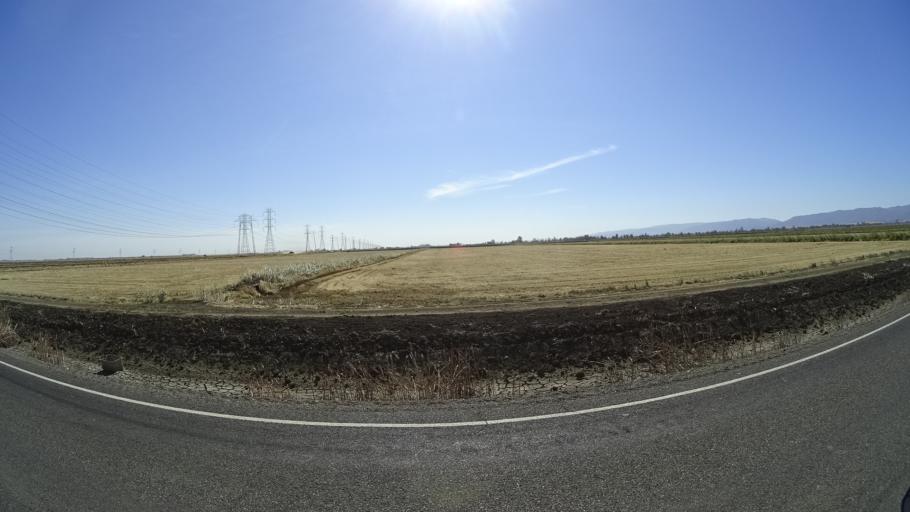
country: US
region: California
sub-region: Yolo County
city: Cottonwood
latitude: 38.6203
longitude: -121.9355
